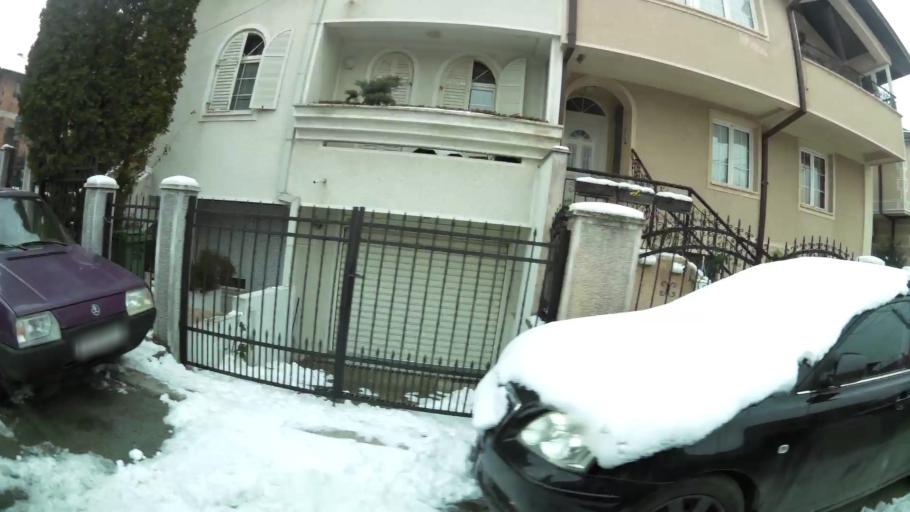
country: MK
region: Saraj
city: Saraj
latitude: 42.0225
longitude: 21.3551
